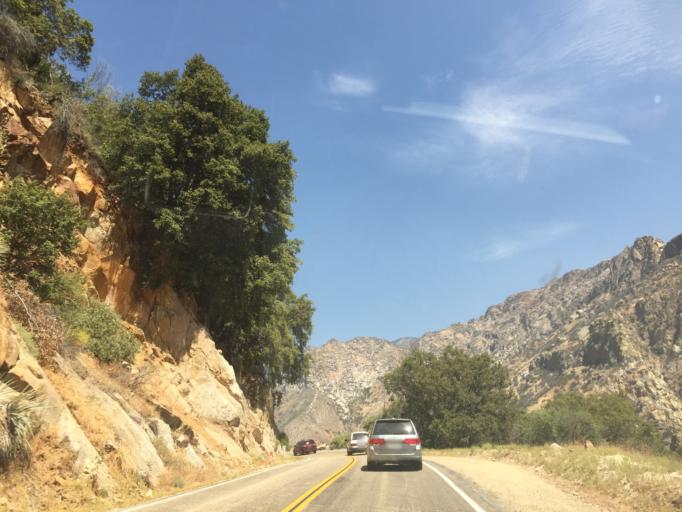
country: US
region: California
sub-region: Tulare County
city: Three Rivers
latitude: 36.8161
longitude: -118.8388
